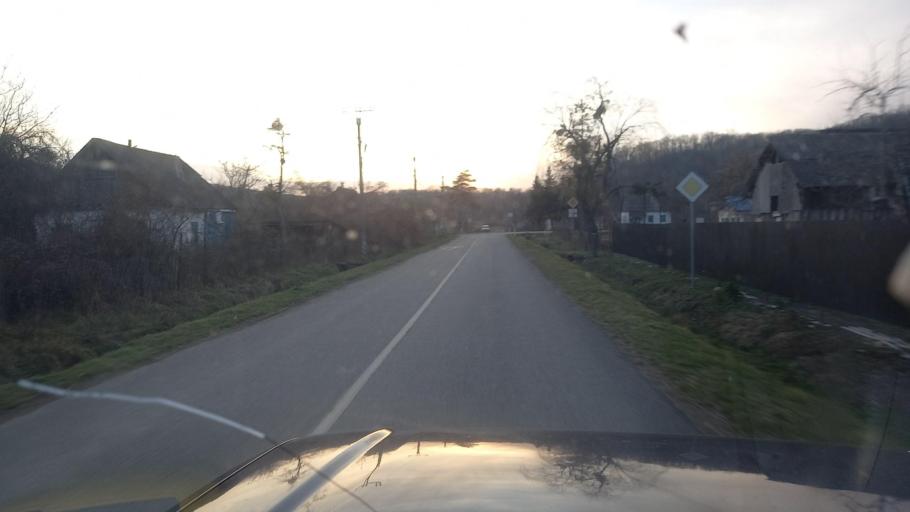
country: RU
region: Krasnodarskiy
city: Goryachiy Klyuch
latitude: 44.3868
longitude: 39.1673
